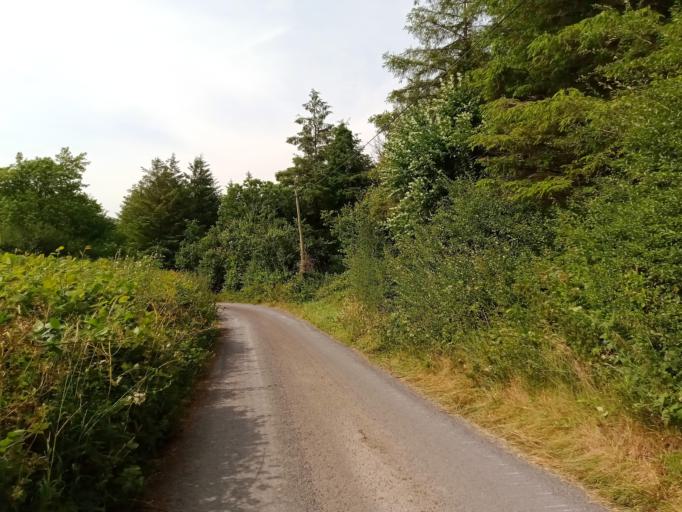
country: IE
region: Leinster
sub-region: Laois
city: Rathdowney
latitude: 52.8004
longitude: -7.4643
